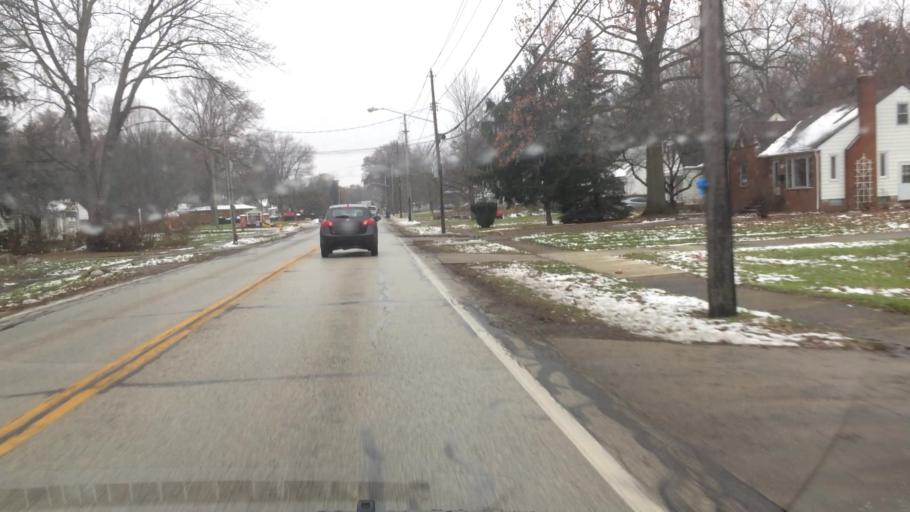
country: US
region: Ohio
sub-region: Cuyahoga County
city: North Olmsted
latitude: 41.4277
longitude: -81.8970
